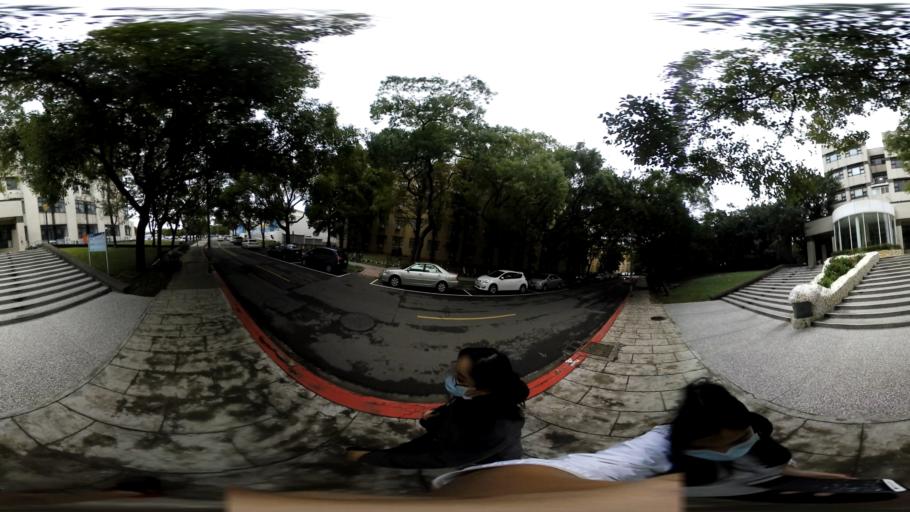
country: TW
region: Taiwan
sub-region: Hsinchu
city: Hsinchu
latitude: 24.7895
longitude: 120.9967
